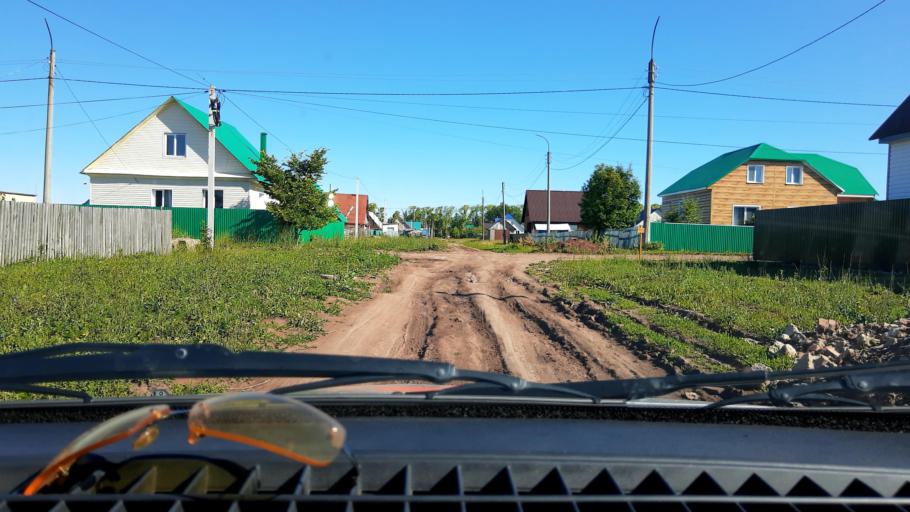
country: RU
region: Bashkortostan
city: Blagoveshchensk
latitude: 55.0638
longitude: 55.9370
